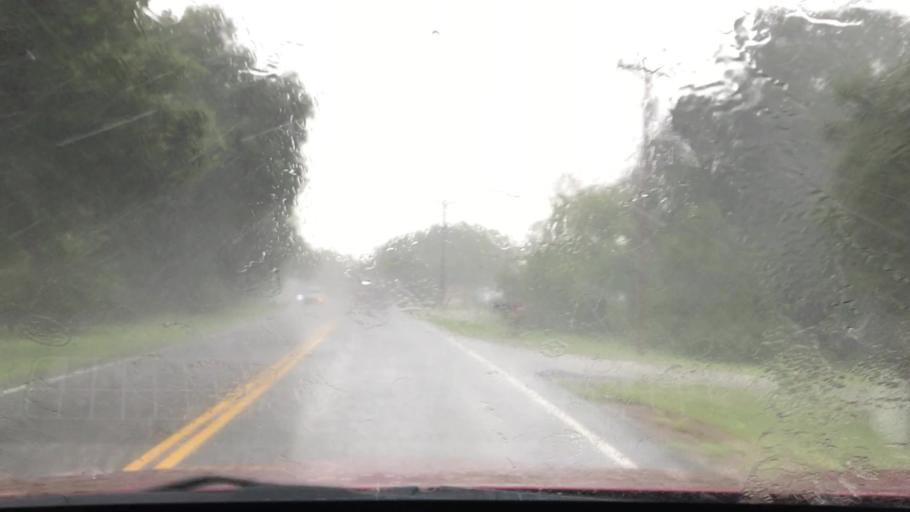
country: US
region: South Carolina
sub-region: Horry County
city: Loris
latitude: 33.9007
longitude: -78.8771
